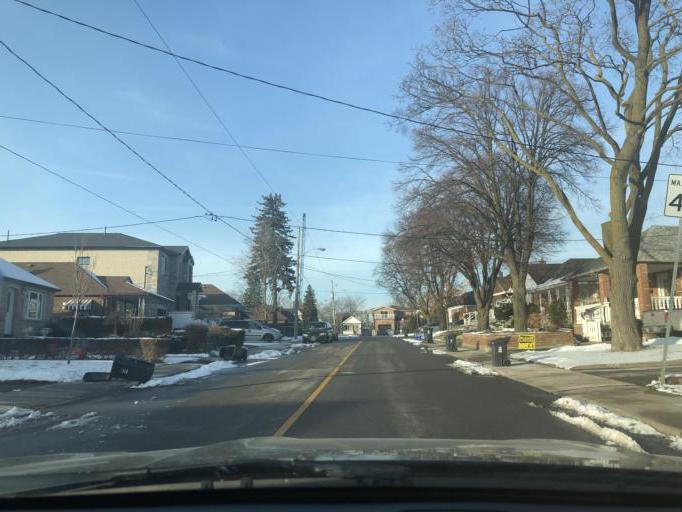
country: CA
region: Ontario
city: Toronto
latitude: 43.6953
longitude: -79.4728
